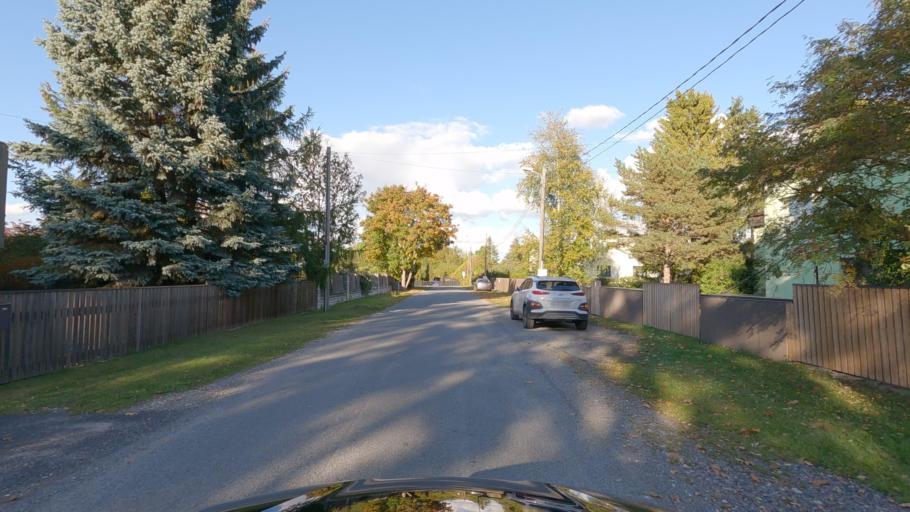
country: EE
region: Harju
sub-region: Saue vald
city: Laagri
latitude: 59.3497
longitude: 24.6306
